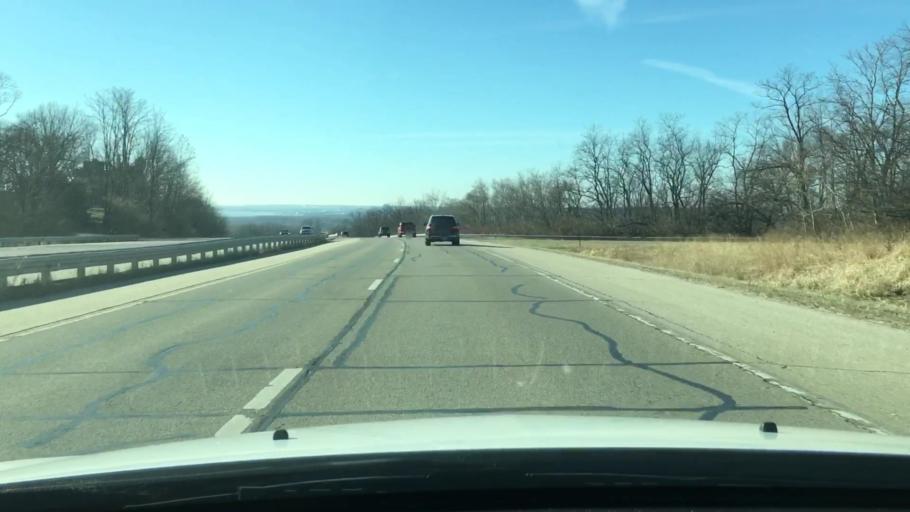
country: US
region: Illinois
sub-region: Woodford County
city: Germantown Hills
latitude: 40.7530
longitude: -89.5040
